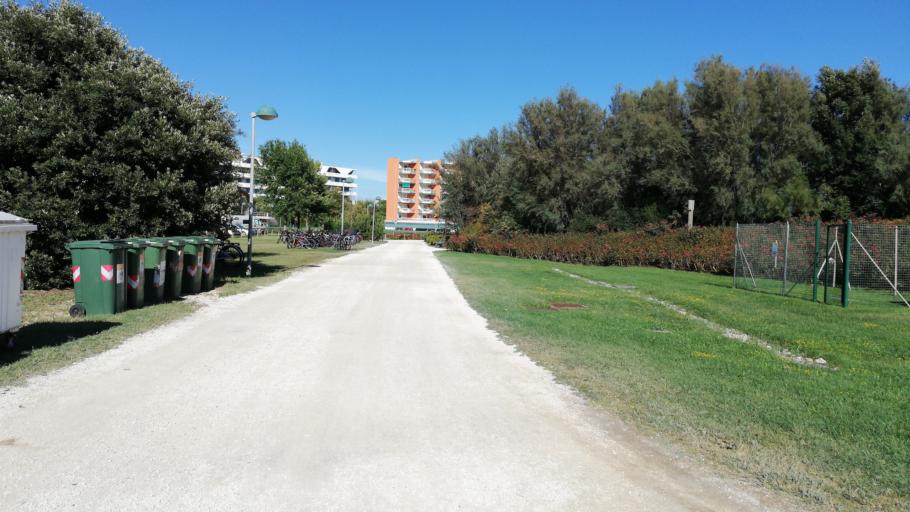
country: IT
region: Veneto
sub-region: Provincia di Venezia
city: Caorle
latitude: 45.5816
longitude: 12.8443
